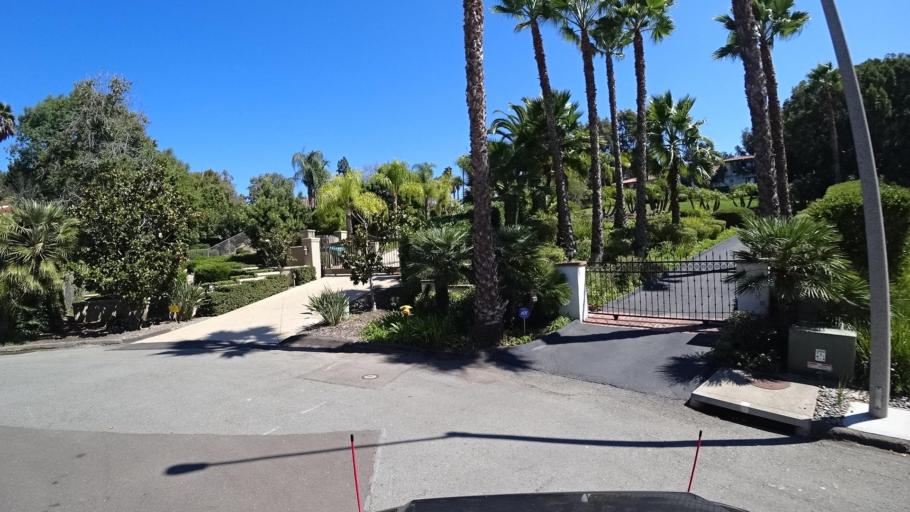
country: US
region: California
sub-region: San Diego County
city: Rancho Santa Fe
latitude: 33.0282
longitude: -117.1727
